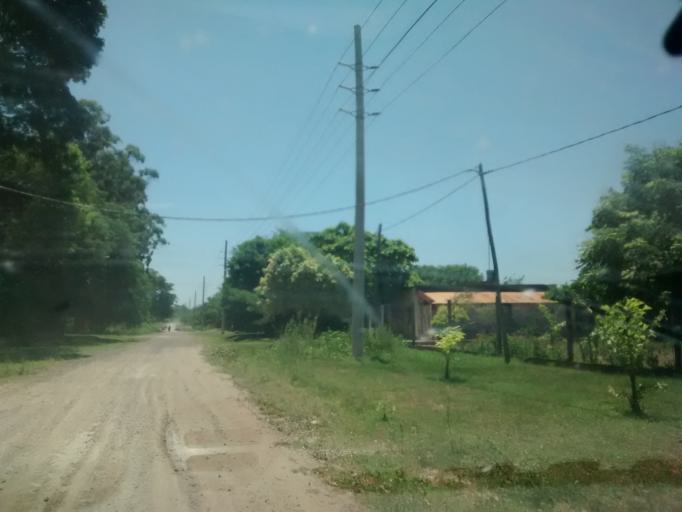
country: AR
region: Chaco
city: Fontana
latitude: -27.4194
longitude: -58.9852
